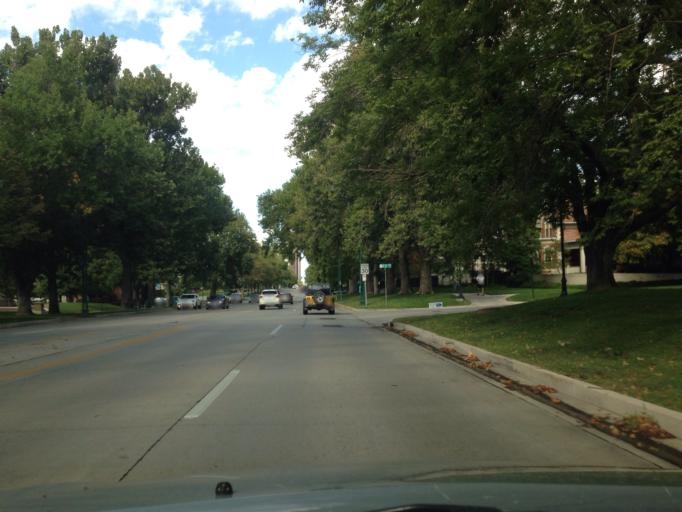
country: US
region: Utah
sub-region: Salt Lake County
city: Salt Lake City
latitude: 40.7694
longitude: -111.8725
